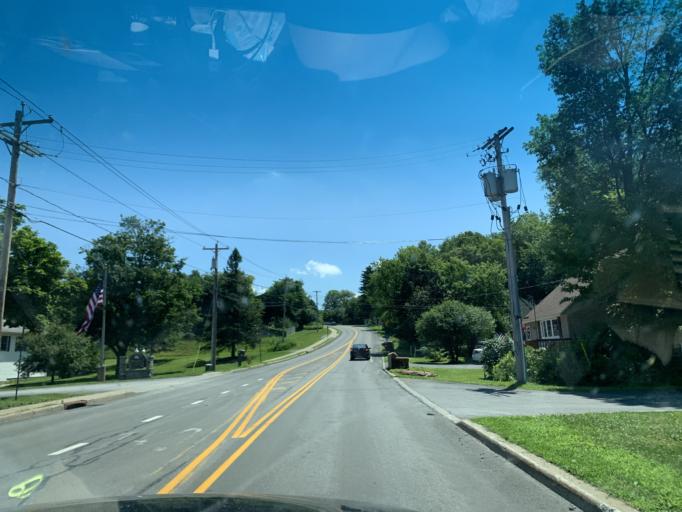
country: US
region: New York
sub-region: Oneida County
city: Washington Mills
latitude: 43.0524
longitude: -75.2710
